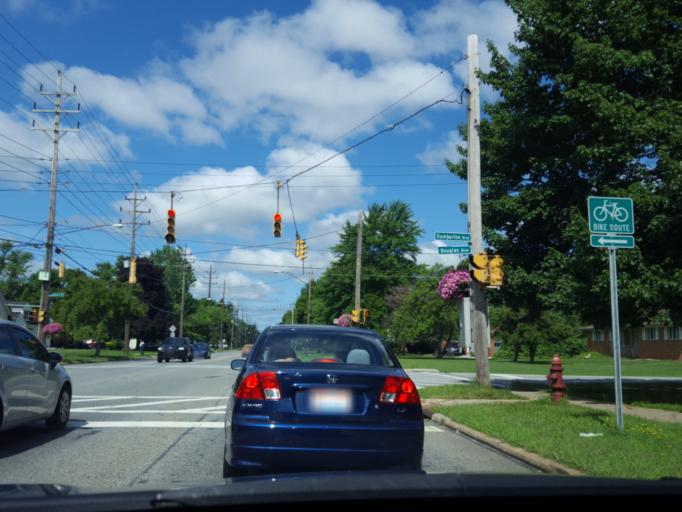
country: US
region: Ohio
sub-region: Cuyahoga County
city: Richmond Heights
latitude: 41.5529
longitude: -81.5098
